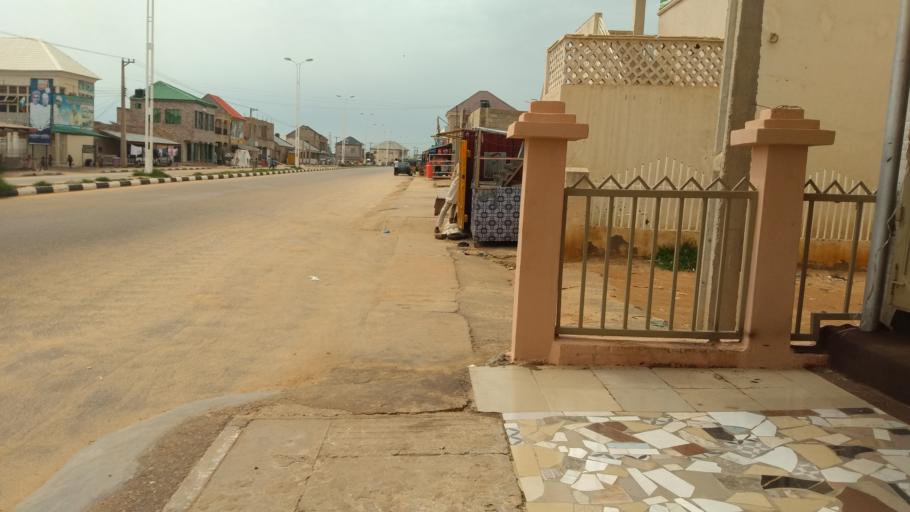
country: NG
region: Katsina
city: Katsina
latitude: 12.9762
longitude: 7.6419
